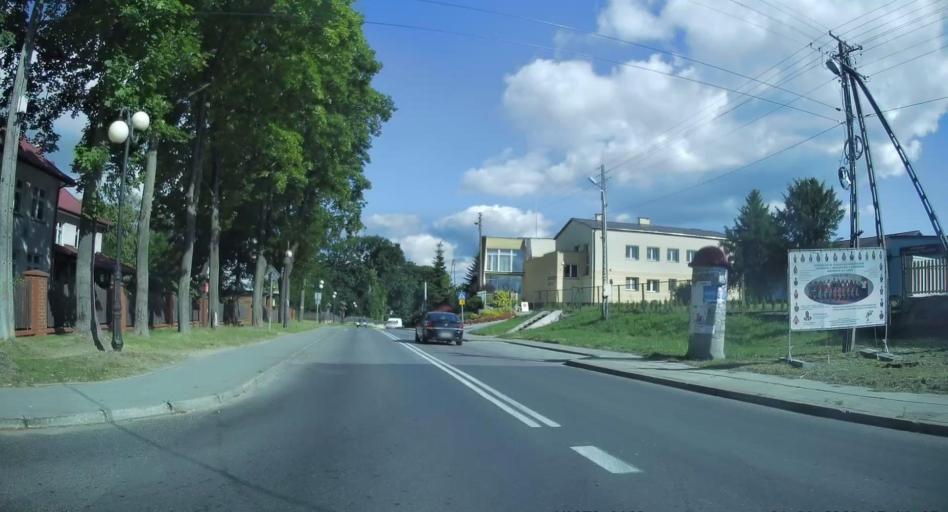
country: PL
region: Swietokrzyskie
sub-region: Powiat kielecki
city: Bodzentyn
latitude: 50.9419
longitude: 20.9473
